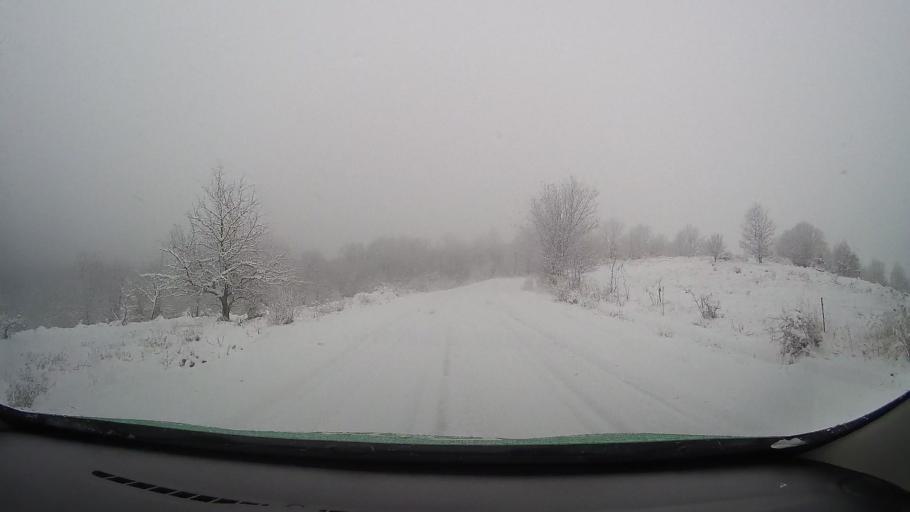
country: RO
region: Hunedoara
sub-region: Comuna Teliucu Inferior
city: Teliucu Inferior
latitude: 45.6928
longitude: 22.8928
